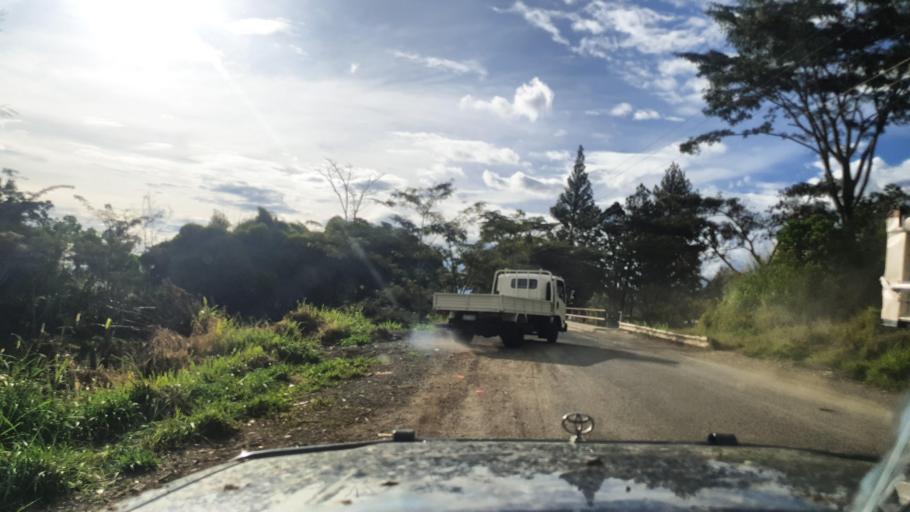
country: PG
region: Jiwaka
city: Minj
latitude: -5.8826
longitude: 144.7227
